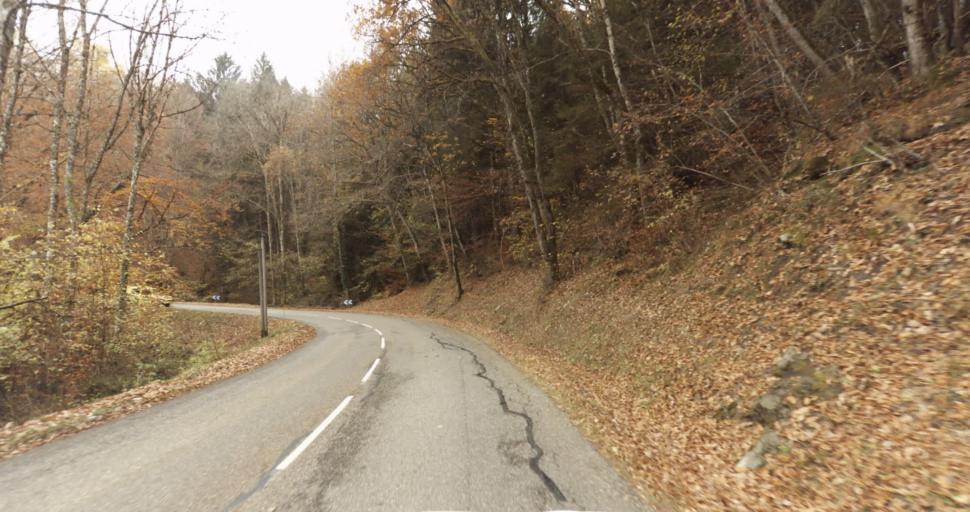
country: FR
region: Rhone-Alpes
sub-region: Departement de la Haute-Savoie
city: Saint-Jorioz
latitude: 45.8010
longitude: 6.1379
